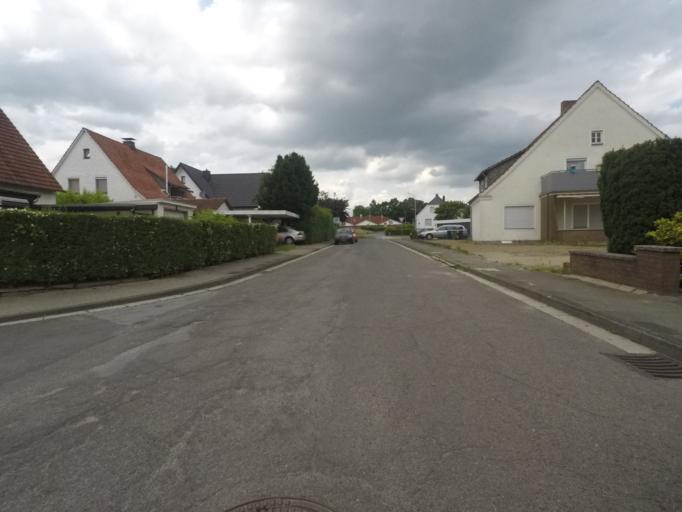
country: DE
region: North Rhine-Westphalia
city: Buende
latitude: 52.2043
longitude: 8.5516
